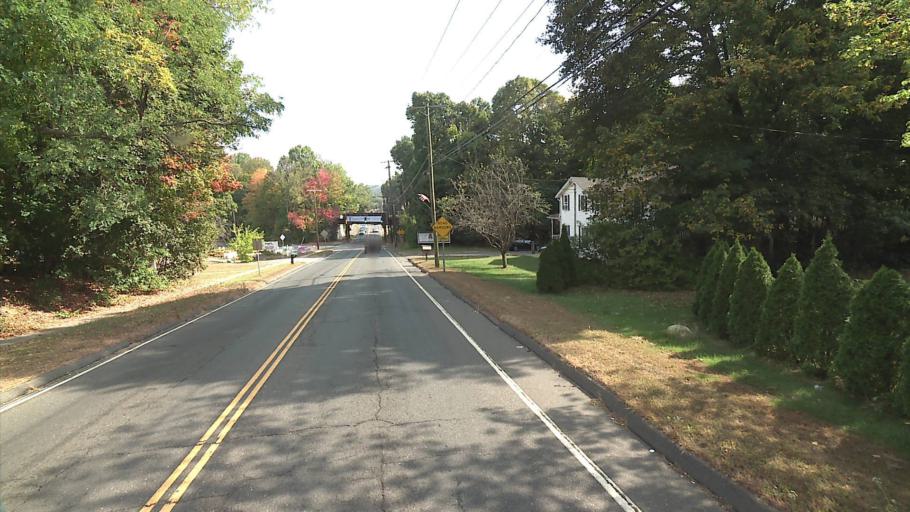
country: US
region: Connecticut
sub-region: Hartford County
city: Bristol
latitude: 41.6809
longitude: -72.9584
